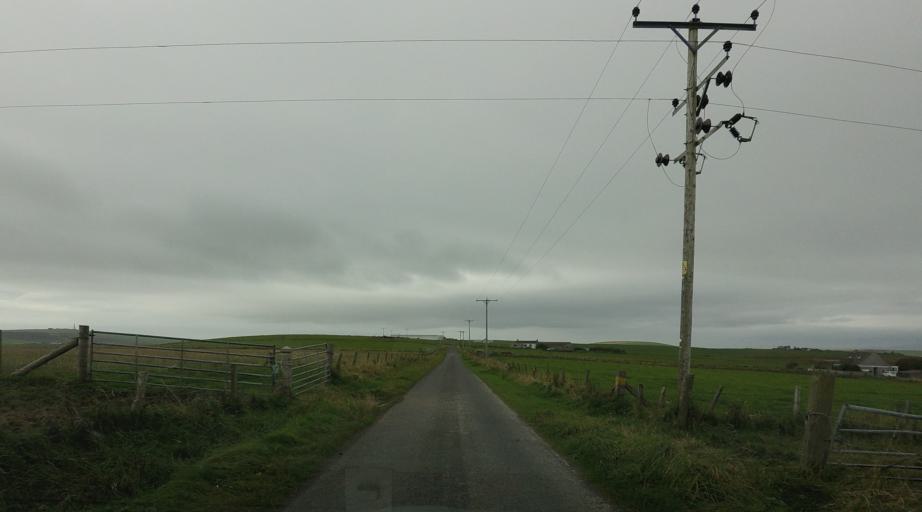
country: GB
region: Scotland
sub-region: Orkney Islands
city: Orkney
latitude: 58.8053
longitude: -2.9379
